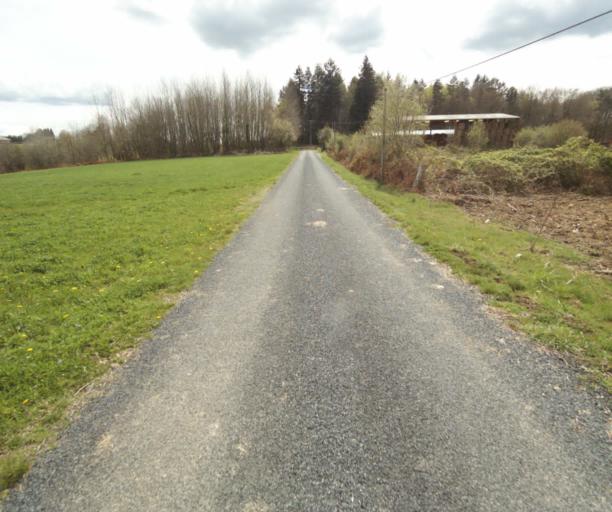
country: FR
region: Limousin
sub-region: Departement de la Correze
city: Laguenne
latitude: 45.2323
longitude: 1.8725
